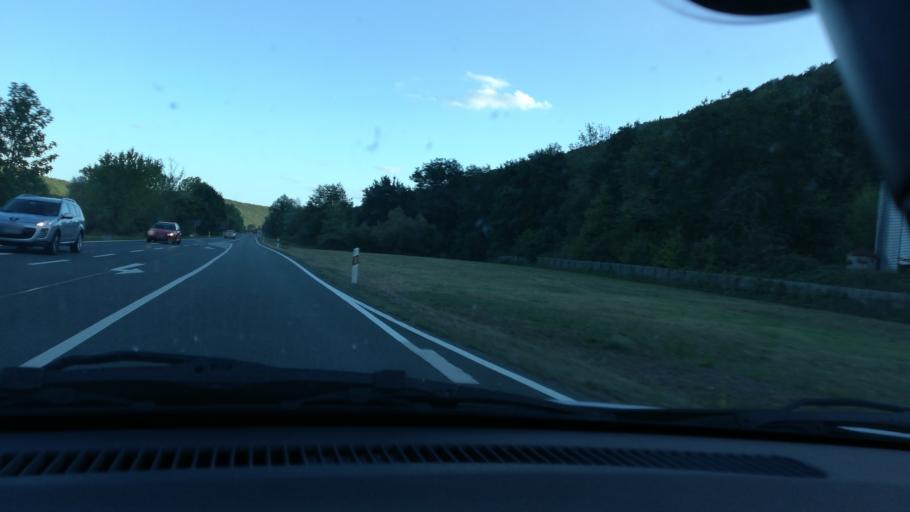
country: DE
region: Bavaria
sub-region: Regierungsbezirk Unterfranken
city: Rothenfels
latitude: 49.8859
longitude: 9.5967
